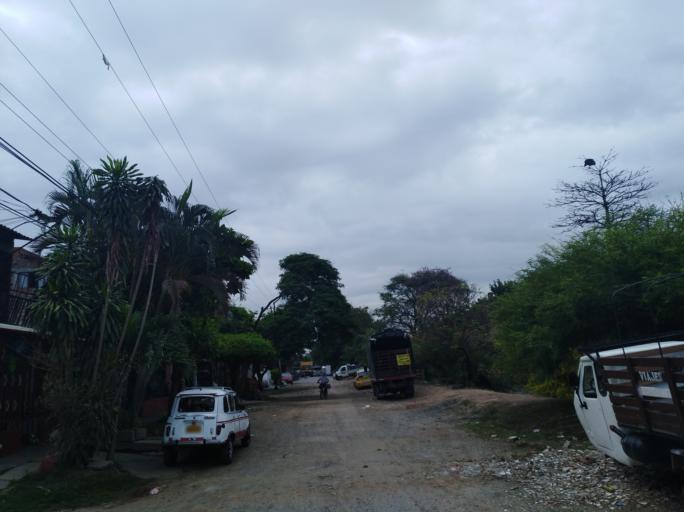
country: CO
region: Valle del Cauca
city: Cali
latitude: 3.4759
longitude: -76.4823
